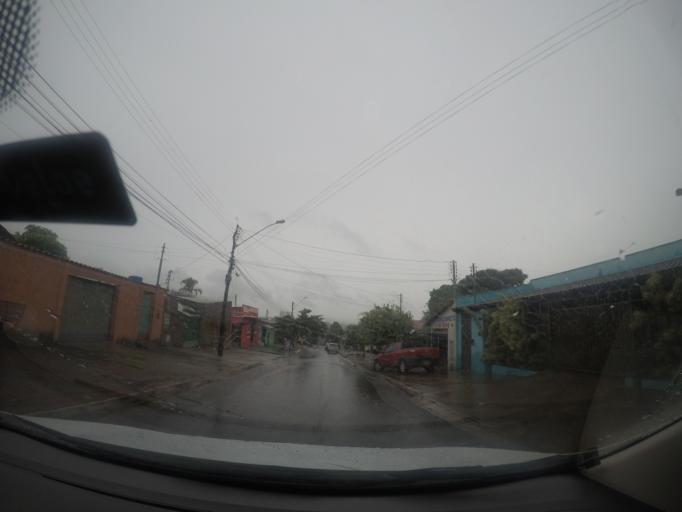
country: BR
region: Goias
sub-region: Goiania
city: Goiania
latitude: -16.6504
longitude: -49.3128
